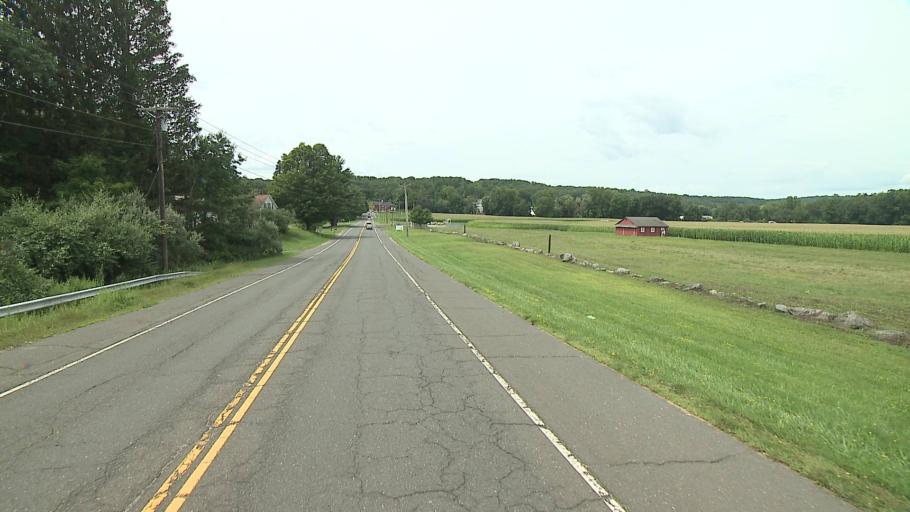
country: US
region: Connecticut
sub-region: Fairfield County
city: Danbury
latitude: 41.4558
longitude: -73.3981
